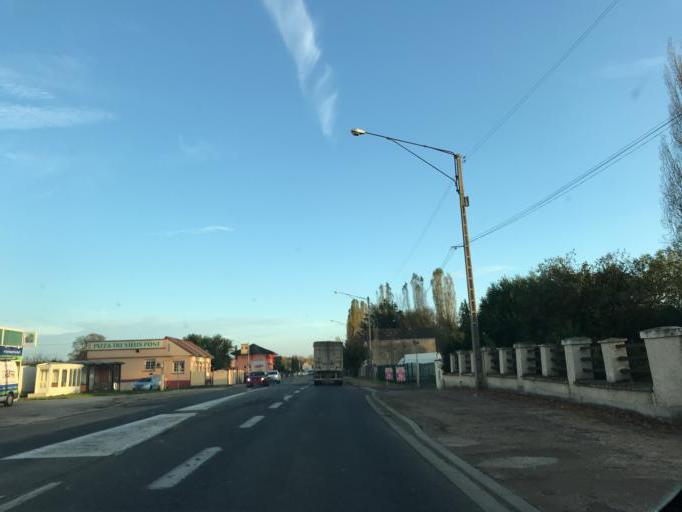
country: FR
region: Bourgogne
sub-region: Departement de l'Yonne
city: Pont-sur-Yonne
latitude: 48.2855
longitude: 3.2100
